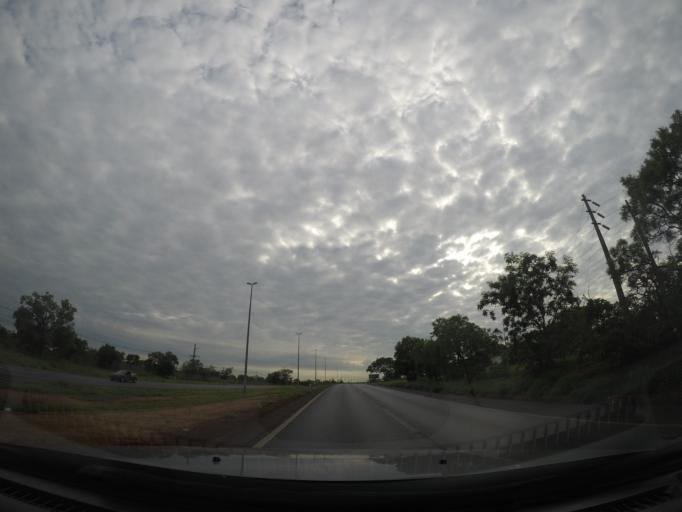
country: BR
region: Goias
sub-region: Planaltina
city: Planaltina
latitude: -15.5947
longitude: -47.6634
